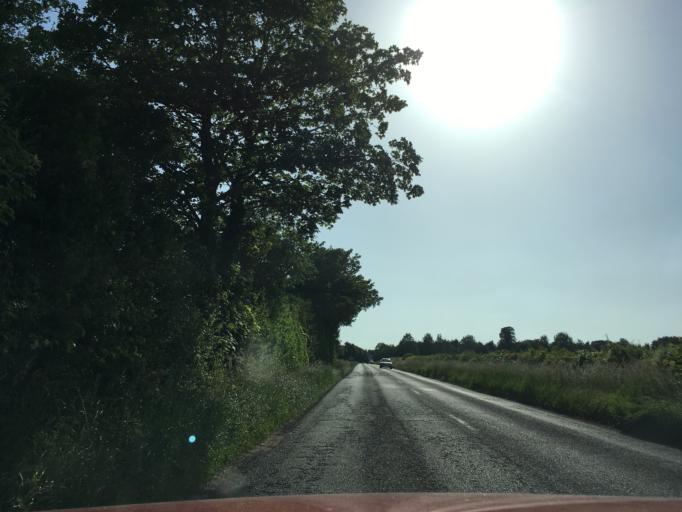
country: GB
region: England
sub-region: Oxfordshire
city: Woodstock
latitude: 51.9261
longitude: -1.3855
